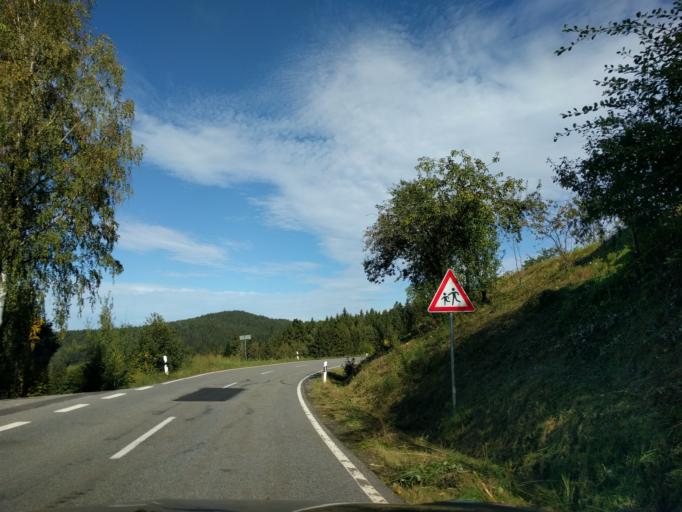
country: DE
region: Bavaria
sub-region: Lower Bavaria
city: Viechtach
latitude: 49.1227
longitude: 12.8862
